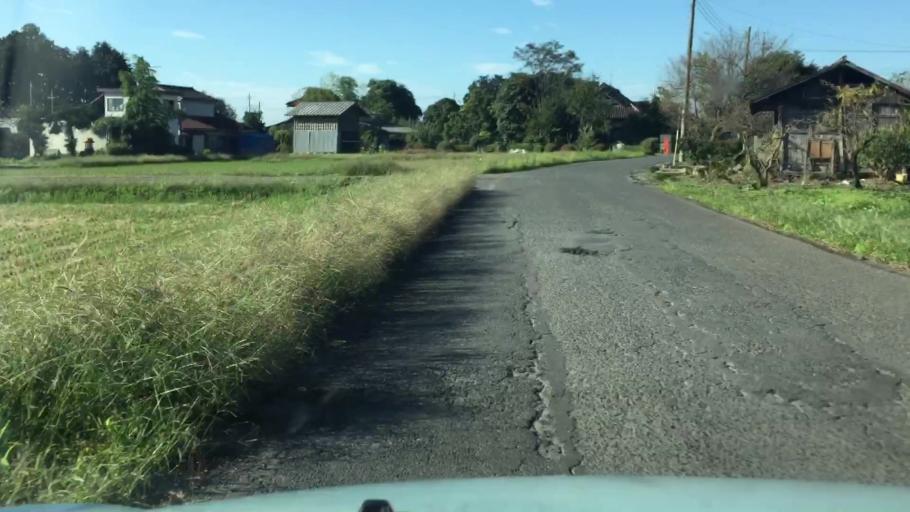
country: JP
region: Tochigi
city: Ujiie
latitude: 36.6930
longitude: 140.0085
